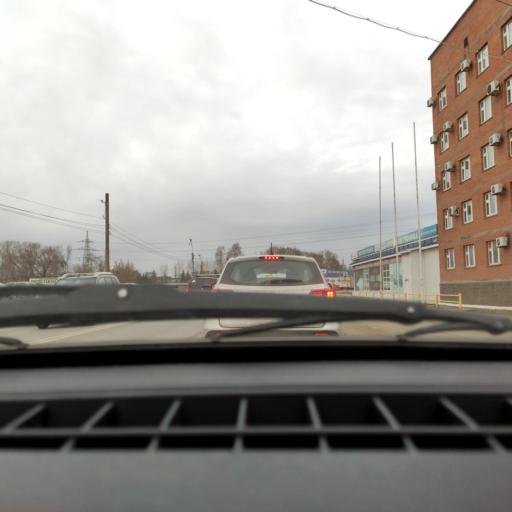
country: RU
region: Bashkortostan
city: Ufa
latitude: 54.7964
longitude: 56.0769
